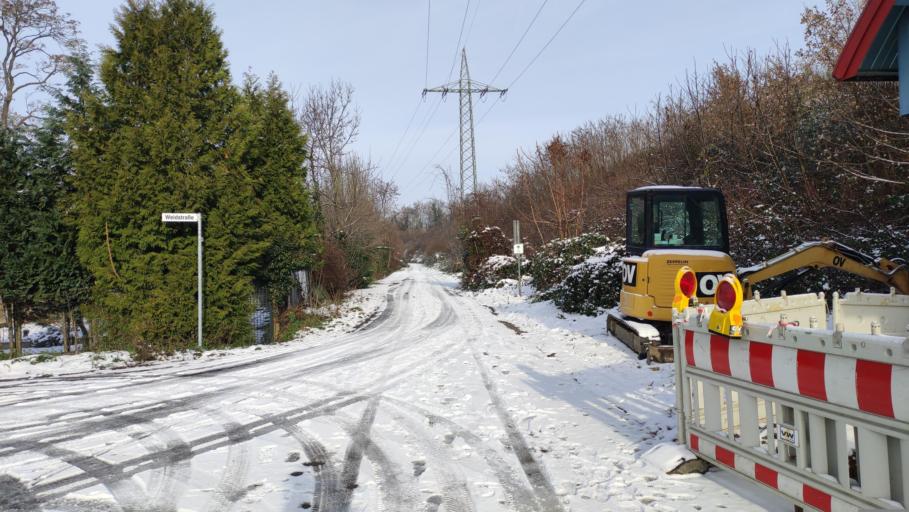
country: DE
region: Baden-Wuerttemberg
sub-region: Freiburg Region
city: Weil am Rhein
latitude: 47.5955
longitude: 7.6073
